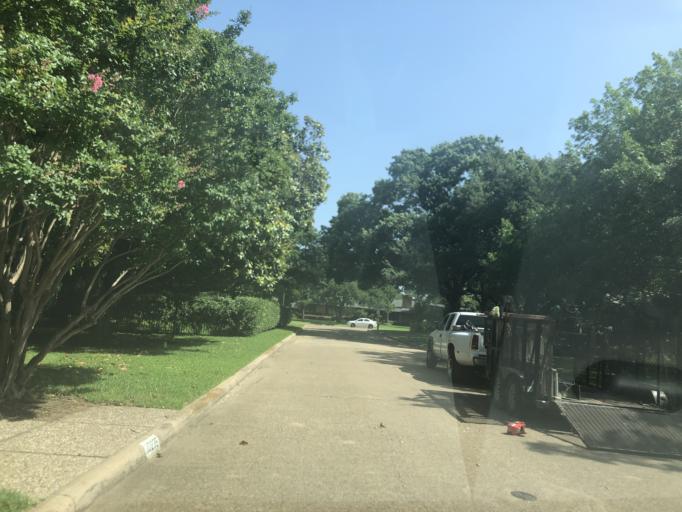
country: US
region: Texas
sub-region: Dallas County
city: University Park
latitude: 32.8843
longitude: -96.8190
